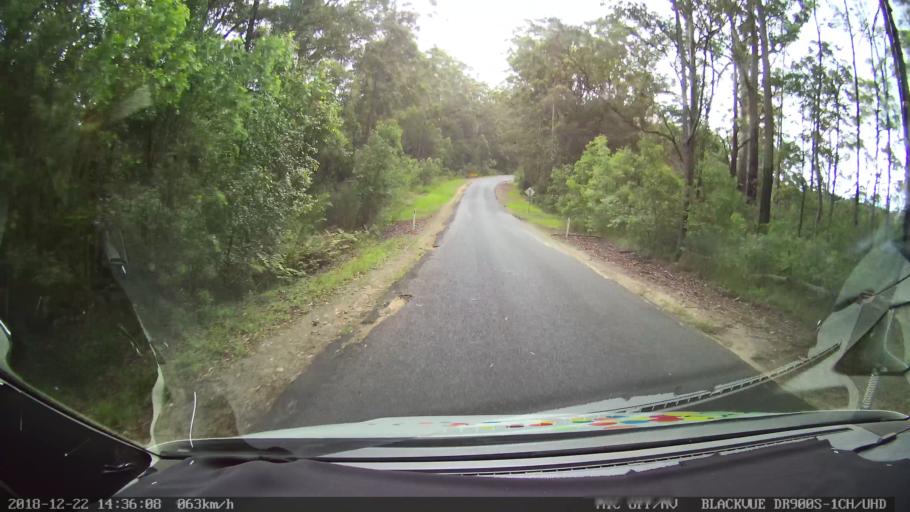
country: AU
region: New South Wales
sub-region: Bellingen
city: Dorrigo
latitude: -30.1267
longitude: 152.6082
